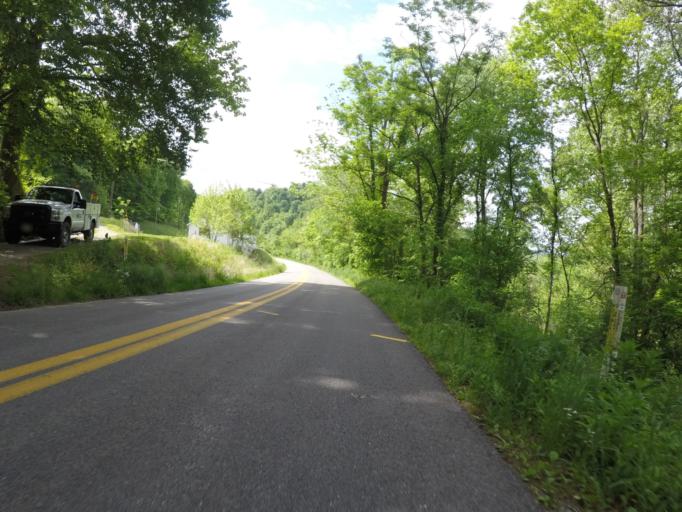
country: US
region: West Virginia
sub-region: Wayne County
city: Ceredo
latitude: 38.3399
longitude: -82.5750
